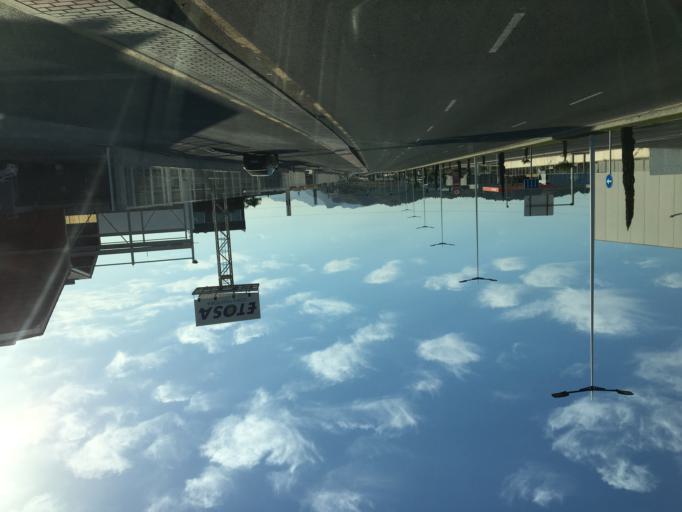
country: ES
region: Murcia
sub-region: Murcia
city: Murcia
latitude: 38.0375
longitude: -1.1173
